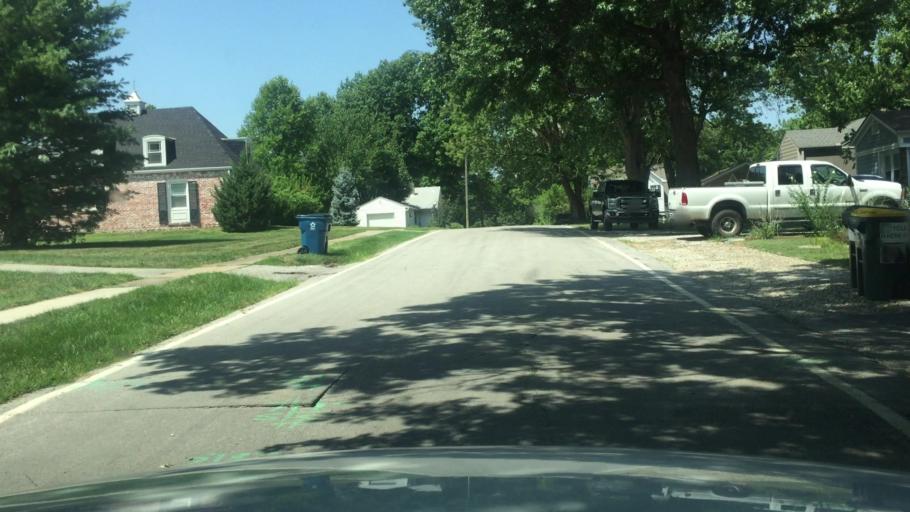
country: US
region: Missouri
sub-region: Jackson County
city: Lees Summit
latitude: 38.9122
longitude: -94.3708
